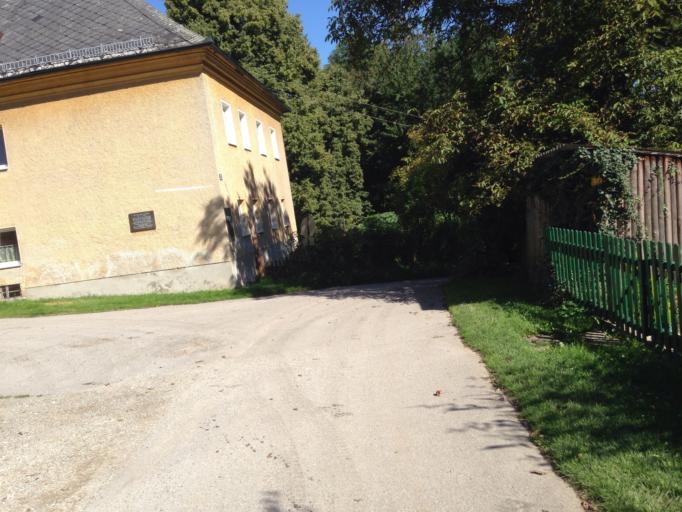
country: AT
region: Upper Austria
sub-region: Politischer Bezirk Linz-Land
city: Leonding
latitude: 48.2857
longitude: 14.2306
